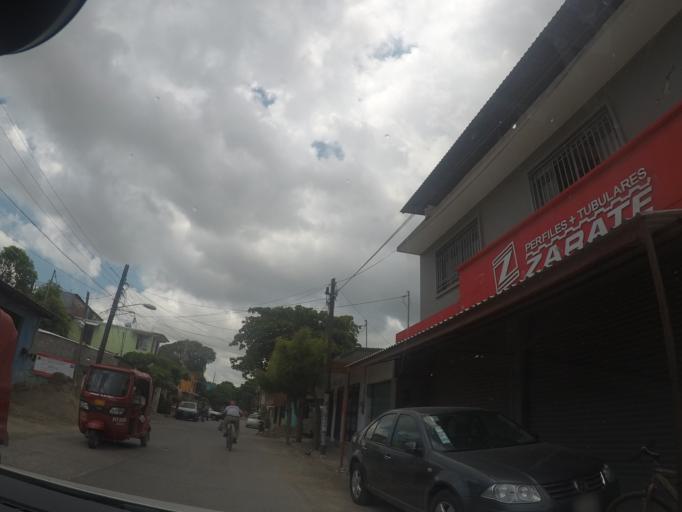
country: MX
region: Oaxaca
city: Juchitan de Zaragoza
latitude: 16.4298
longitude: -95.0229
